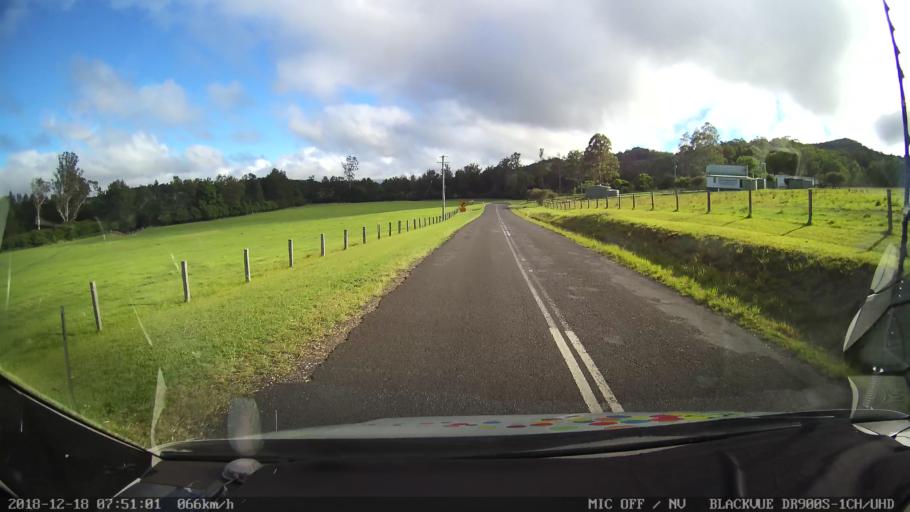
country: AU
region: New South Wales
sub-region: Kyogle
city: Kyogle
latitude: -28.4402
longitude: 152.5749
